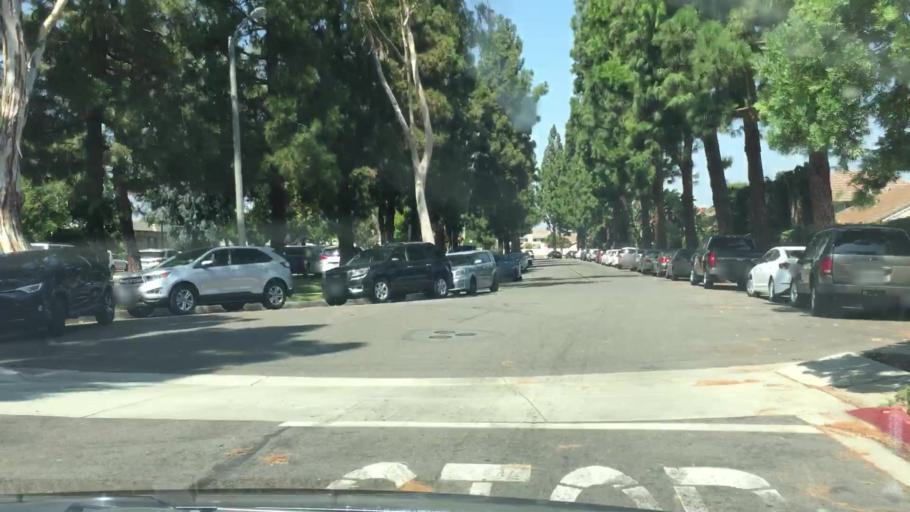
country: US
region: California
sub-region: Orange County
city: Irvine
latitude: 33.6858
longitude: -117.7855
